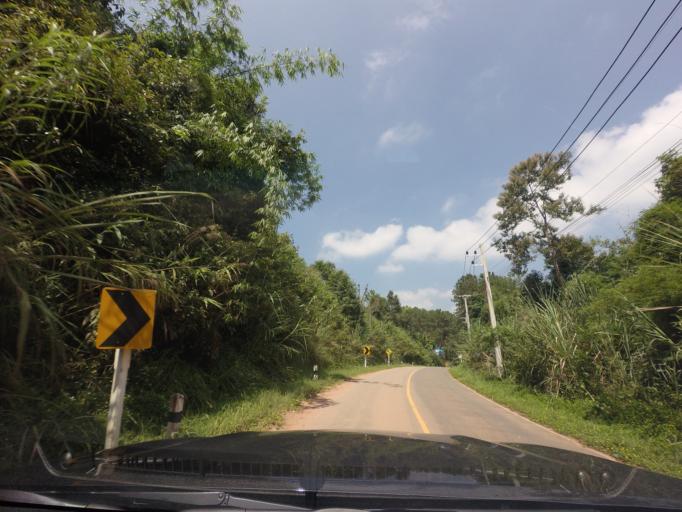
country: TH
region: Loei
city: Na Haeo
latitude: 17.4666
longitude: 100.9261
